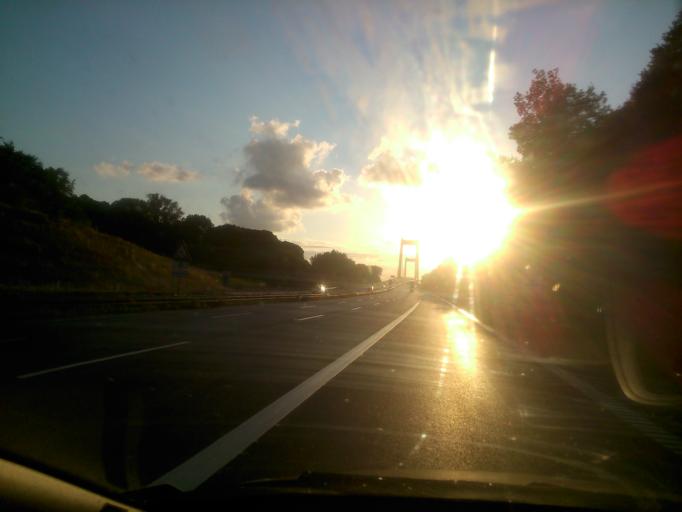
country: DK
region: South Denmark
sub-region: Middelfart Kommune
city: Strib
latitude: 55.5148
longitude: 9.7688
